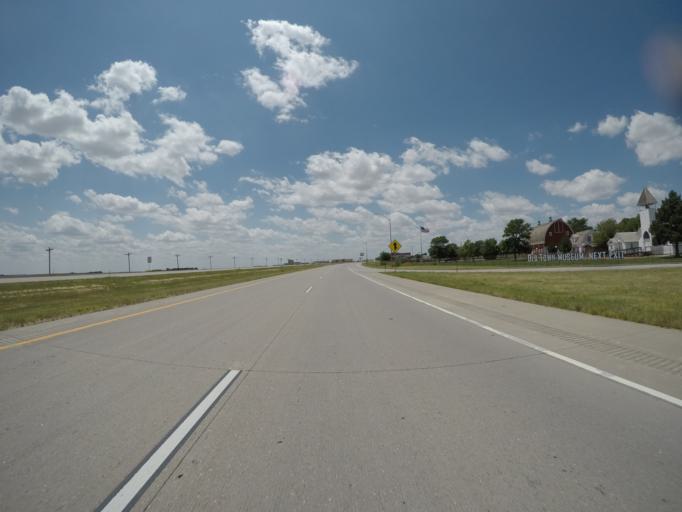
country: US
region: Colorado
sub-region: Kit Carson County
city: Burlington
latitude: 39.2952
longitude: -102.2663
